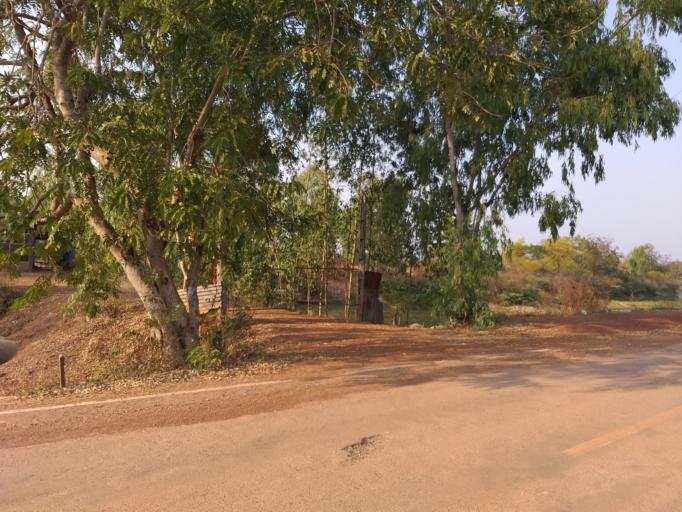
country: TH
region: Changwat Udon Thani
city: Ban Dung
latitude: 17.7442
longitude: 103.3558
